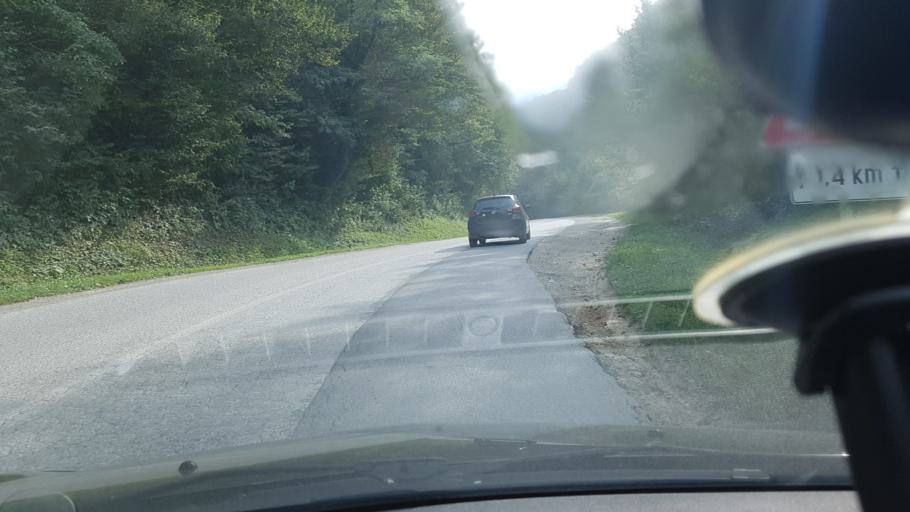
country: HR
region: Varazdinska
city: Lepoglava
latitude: 46.1883
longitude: 15.9853
